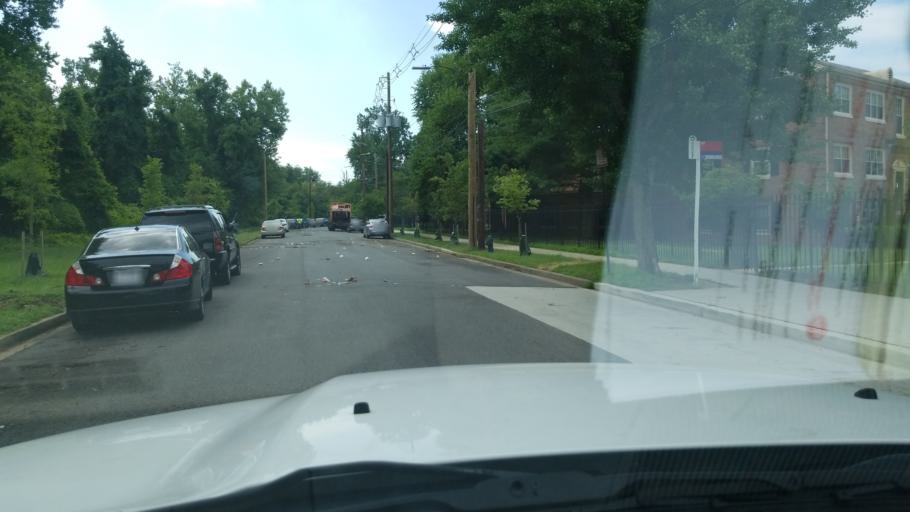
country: US
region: Maryland
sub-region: Prince George's County
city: Colmar Manor
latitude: 38.9041
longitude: -76.9473
